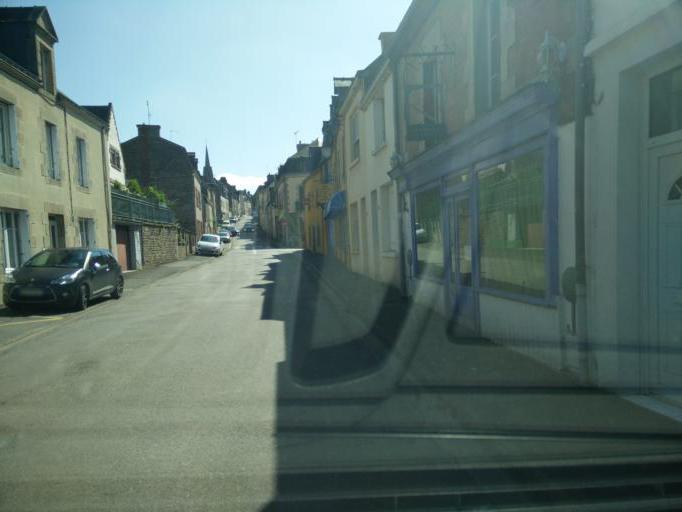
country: FR
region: Brittany
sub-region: Departement du Morbihan
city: Josselin
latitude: 47.9531
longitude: -2.5527
